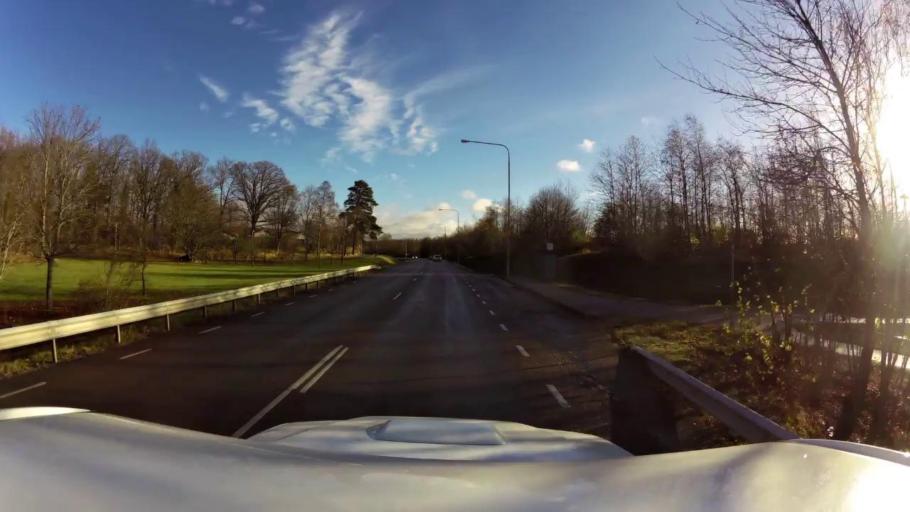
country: SE
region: OEstergoetland
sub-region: Linkopings Kommun
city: Sturefors
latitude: 58.3726
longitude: 15.6794
